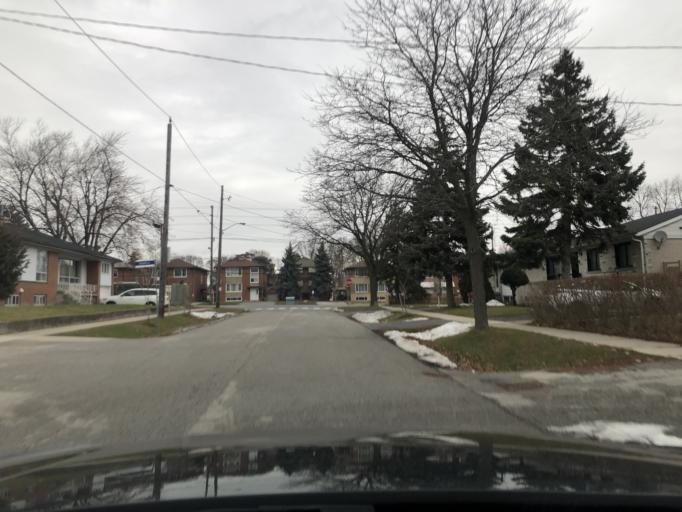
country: CA
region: Ontario
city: Etobicoke
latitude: 43.6985
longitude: -79.5370
